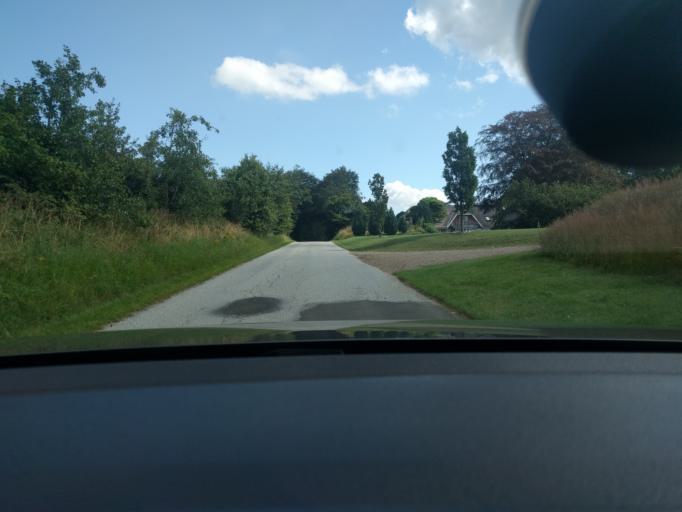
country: DK
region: Central Jutland
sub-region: Viborg Kommune
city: Viborg
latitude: 56.4995
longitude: 9.2939
